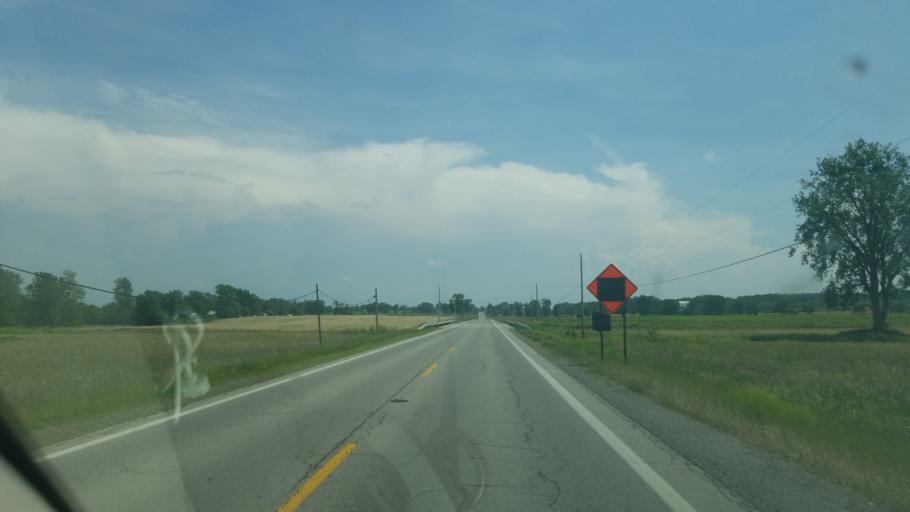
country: US
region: Ohio
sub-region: Logan County
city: Northwood
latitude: 40.4967
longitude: -83.7425
